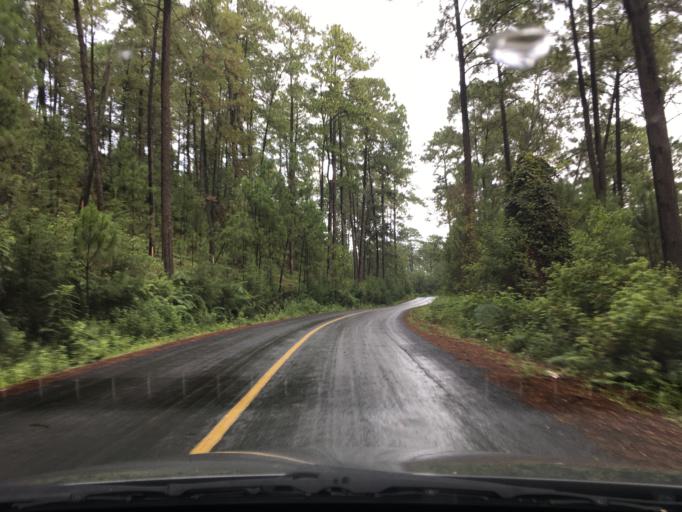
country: MX
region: Michoacan
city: Nuevo San Juan Parangaricutiro
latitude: 19.4379
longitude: -102.1499
